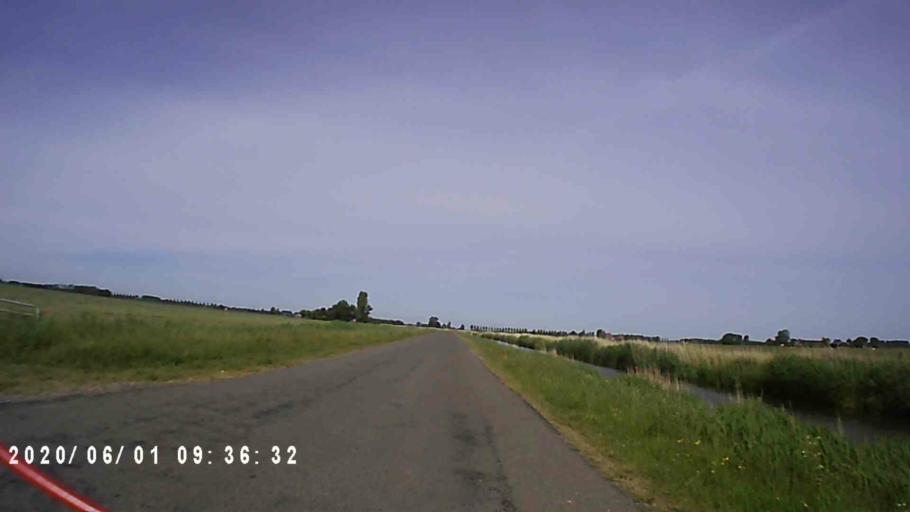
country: NL
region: Friesland
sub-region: Gemeente Het Bildt
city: Sint Annaparochie
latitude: 53.2603
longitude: 5.6987
